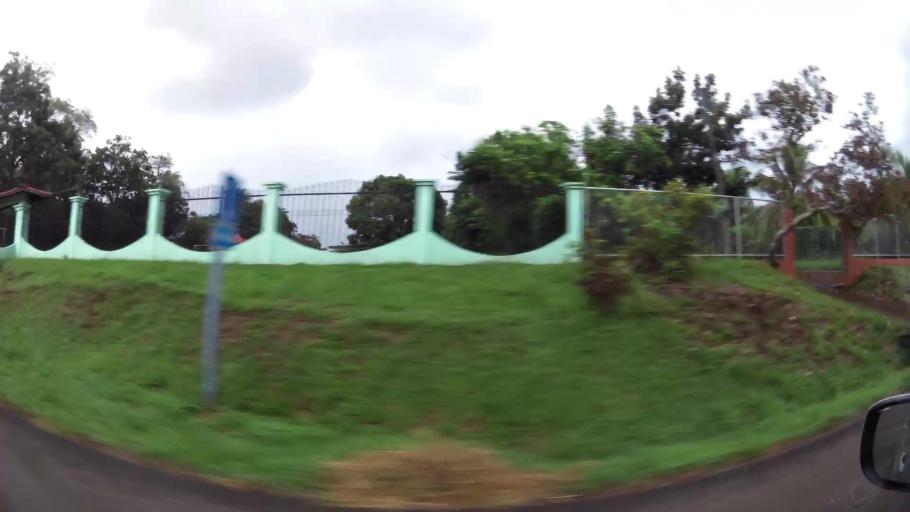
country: CR
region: Puntarenas
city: Esparza
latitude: 9.9721
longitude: -84.6171
